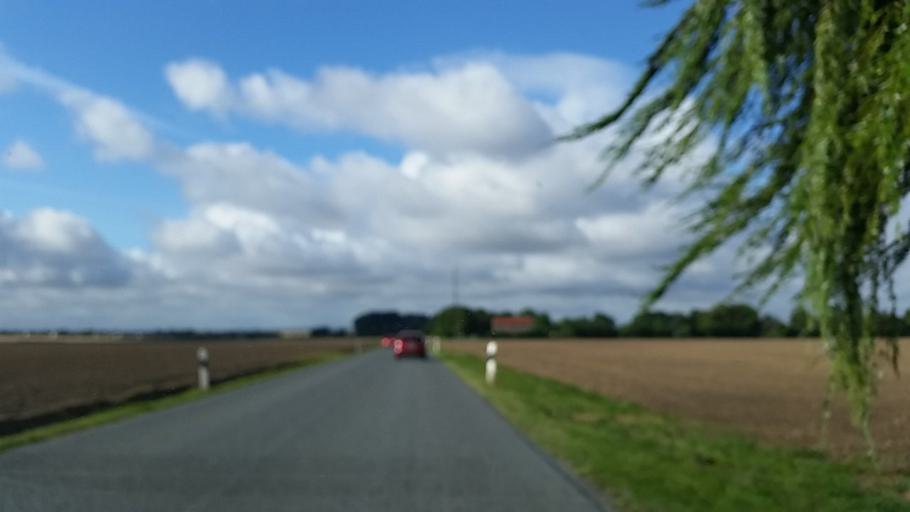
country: DE
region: Lower Saxony
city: Sickte
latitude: 52.2087
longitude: 10.6322
